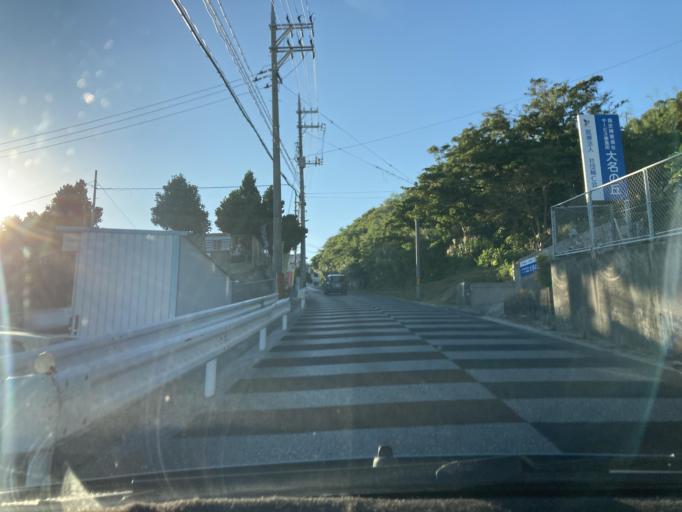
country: JP
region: Okinawa
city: Naha-shi
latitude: 26.2106
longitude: 127.7322
